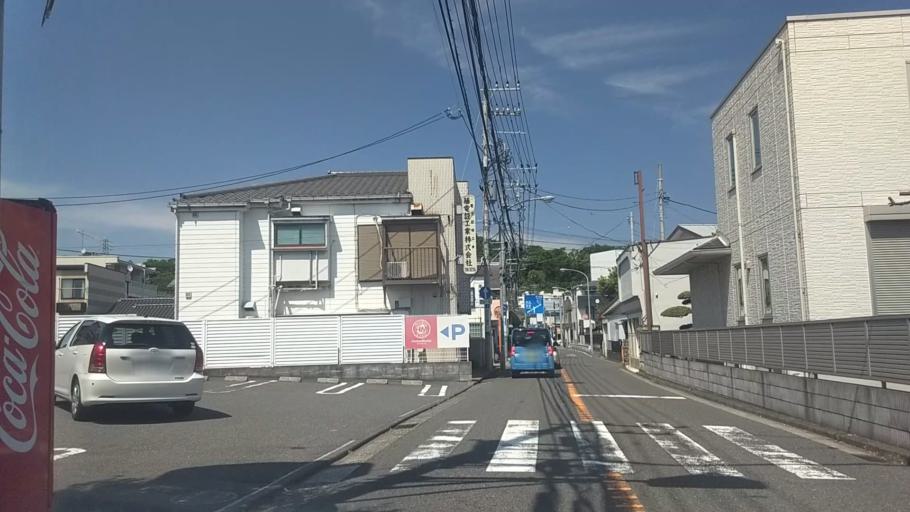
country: JP
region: Kanagawa
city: Zushi
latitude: 35.3268
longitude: 139.6136
